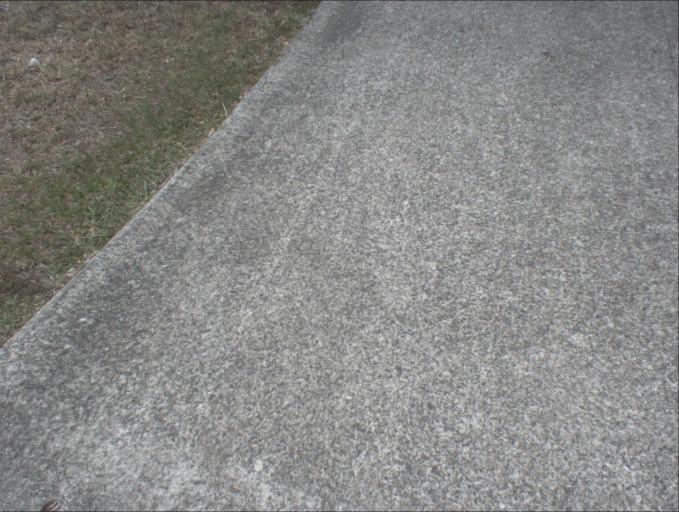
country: AU
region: Queensland
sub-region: Logan
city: Slacks Creek
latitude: -27.6568
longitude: 153.1652
